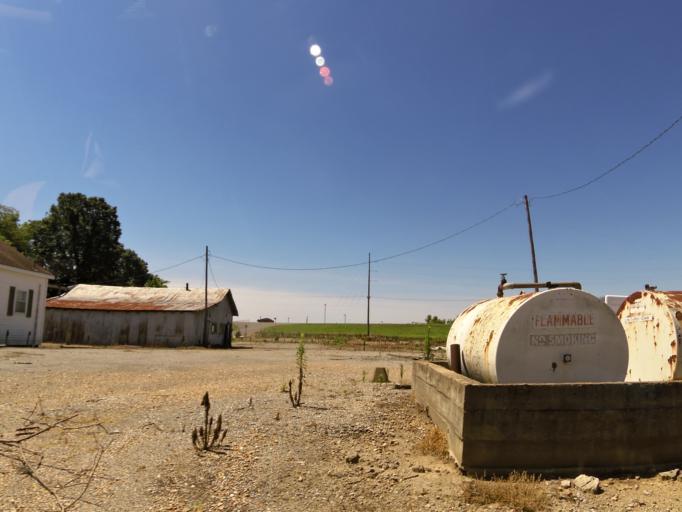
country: US
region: Missouri
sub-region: New Madrid County
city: New Madrid
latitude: 36.5846
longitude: -89.5356
